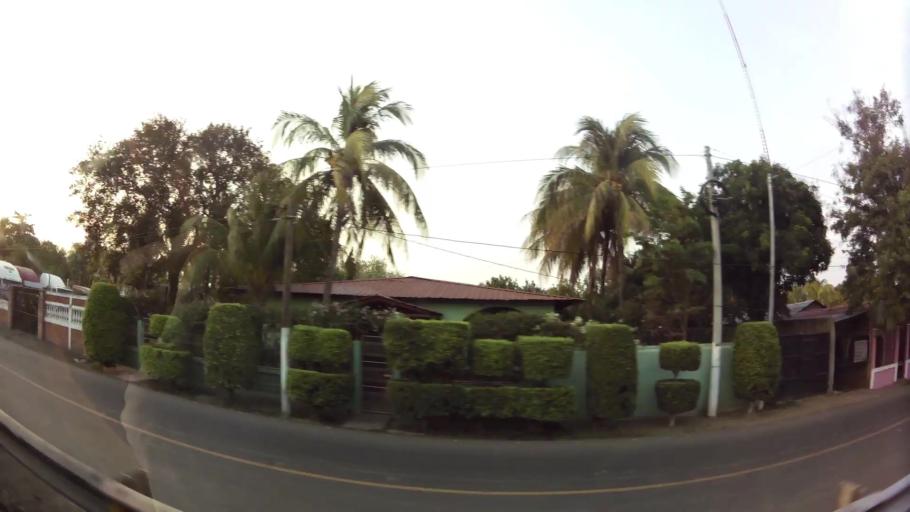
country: NI
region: Leon
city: La Paz Centro
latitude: 12.3350
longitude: -86.6736
